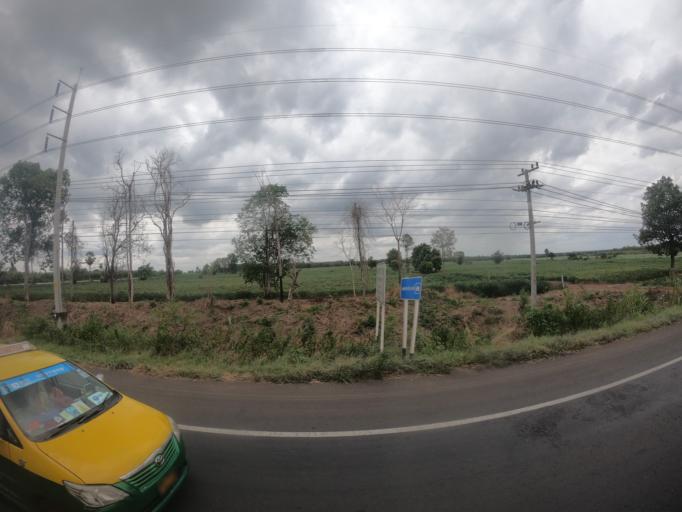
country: TH
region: Buriram
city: Nong Ki
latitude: 14.7097
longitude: 102.4637
